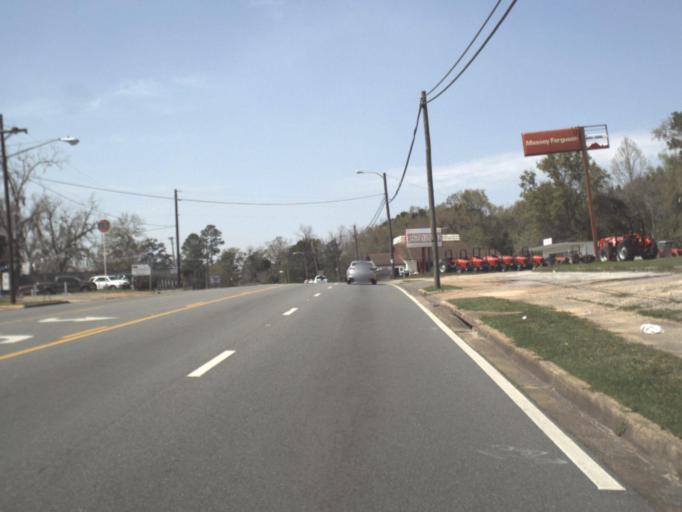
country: US
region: Florida
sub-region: Gadsden County
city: Quincy
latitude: 30.5862
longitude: -84.5671
